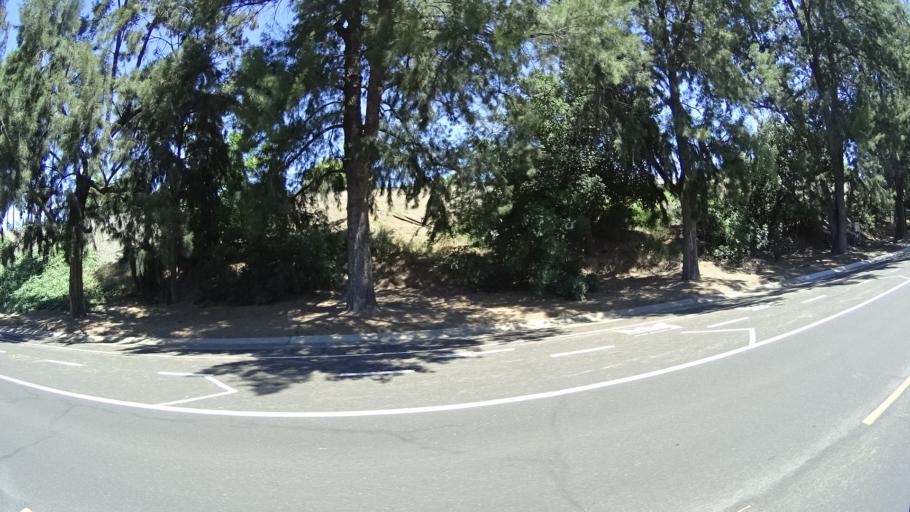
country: US
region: California
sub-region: Sacramento County
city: Sacramento
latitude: 38.5815
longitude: -121.4449
